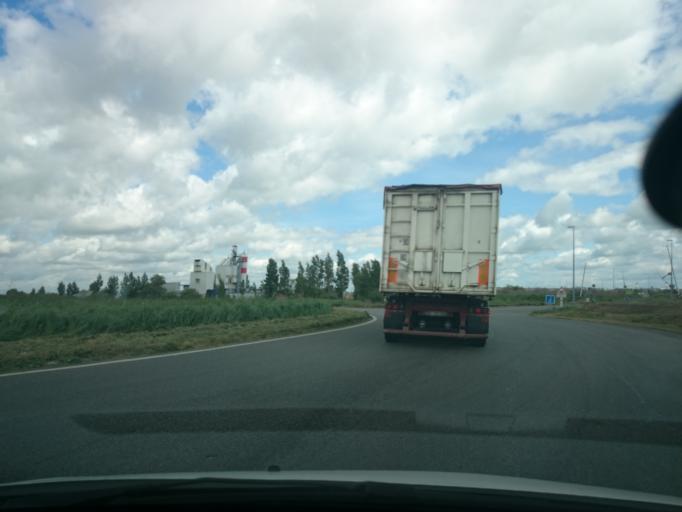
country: FR
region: Pays de la Loire
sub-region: Departement de la Loire-Atlantique
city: Montoir-de-Bretagne
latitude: 47.3181
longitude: -2.1170
